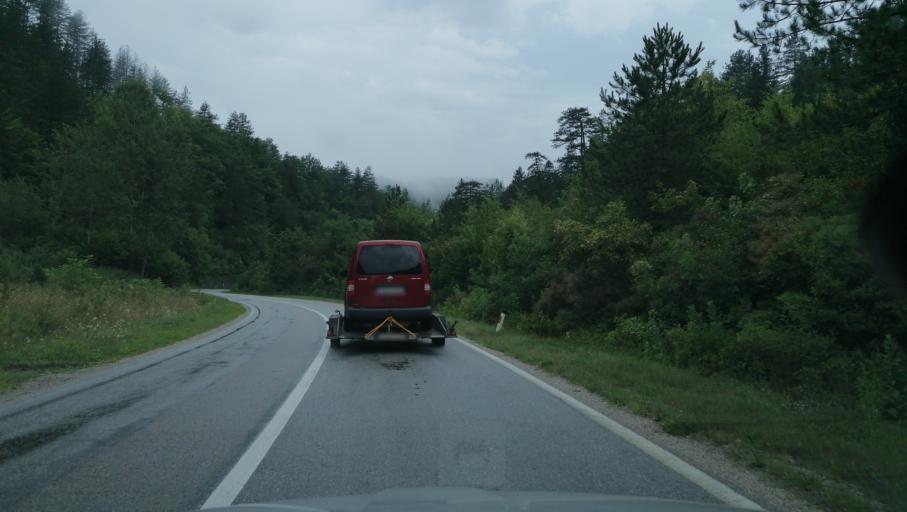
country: RS
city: Durici
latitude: 43.7778
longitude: 19.3748
